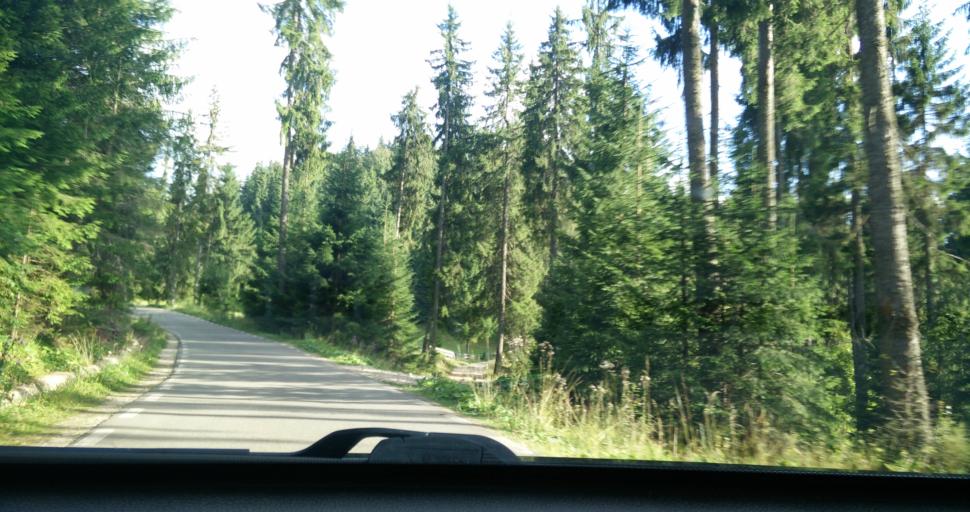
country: RO
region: Alba
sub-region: Comuna Scarisoara
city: Scarisoara
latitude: 46.4878
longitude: 22.8255
